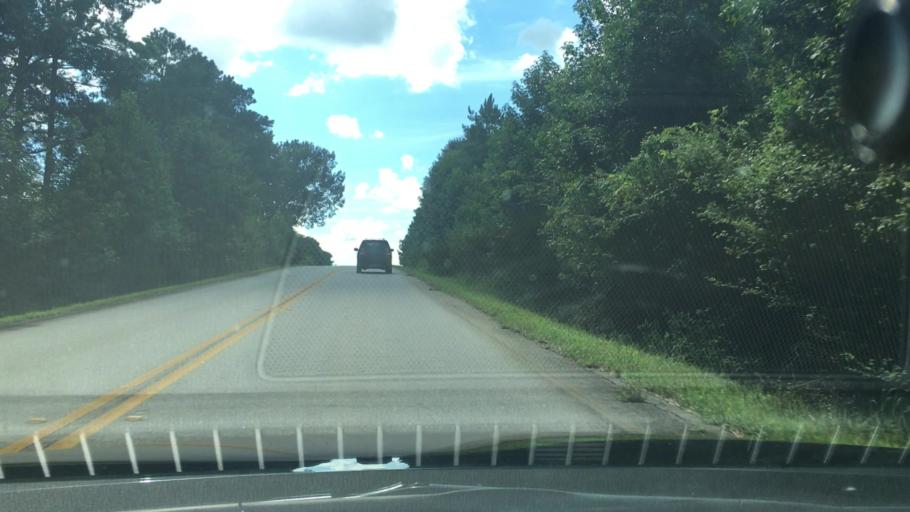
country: US
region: Georgia
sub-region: Jasper County
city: Monticello
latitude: 33.3019
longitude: -83.6413
